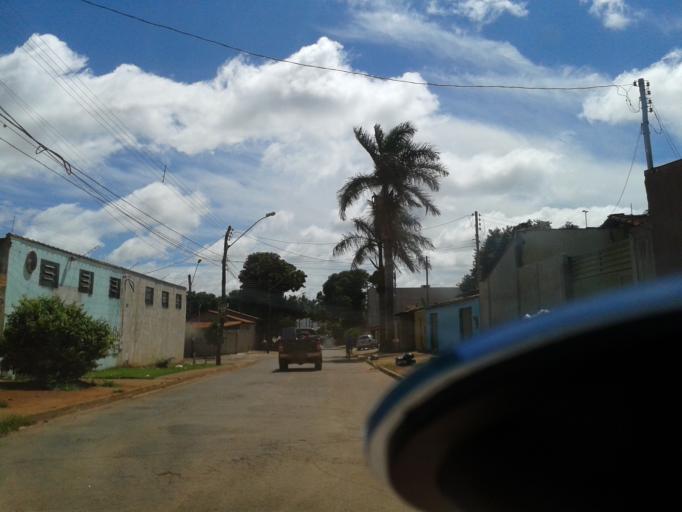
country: BR
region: Goias
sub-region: Goiania
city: Goiania
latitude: -16.6511
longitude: -49.3389
